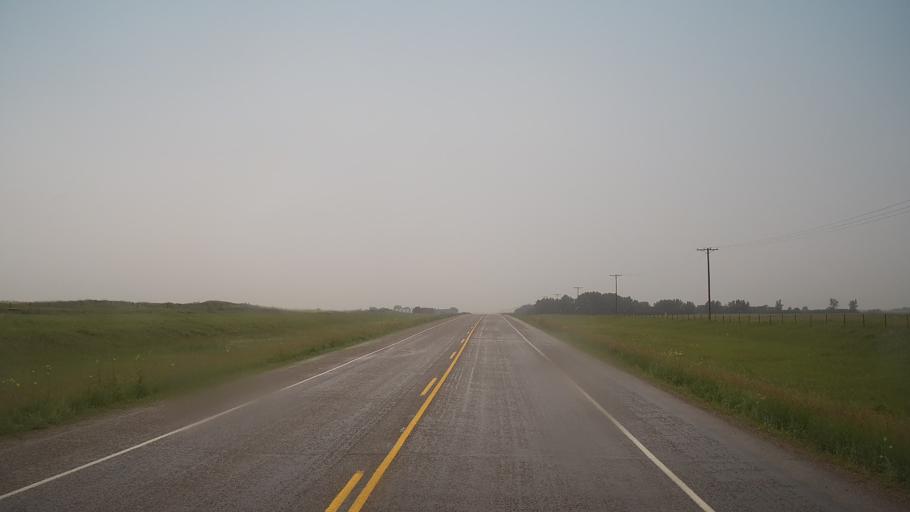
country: CA
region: Saskatchewan
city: Biggar
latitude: 52.1330
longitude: -108.1572
